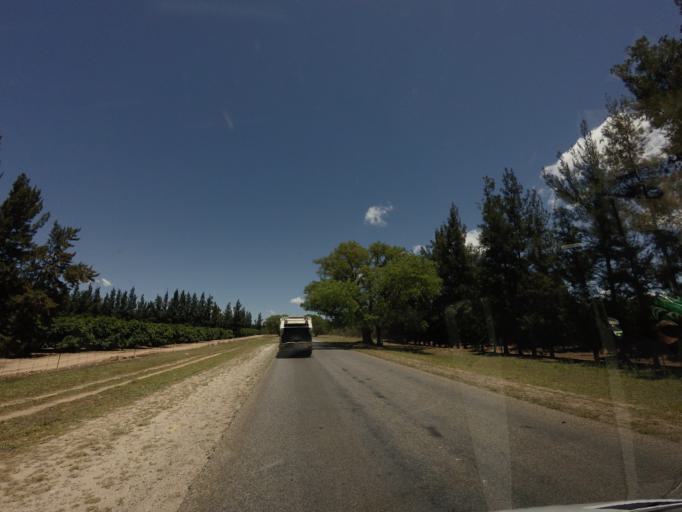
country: ZA
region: Limpopo
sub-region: Mopani District Municipality
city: Hoedspruit
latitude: -24.4033
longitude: 30.7763
